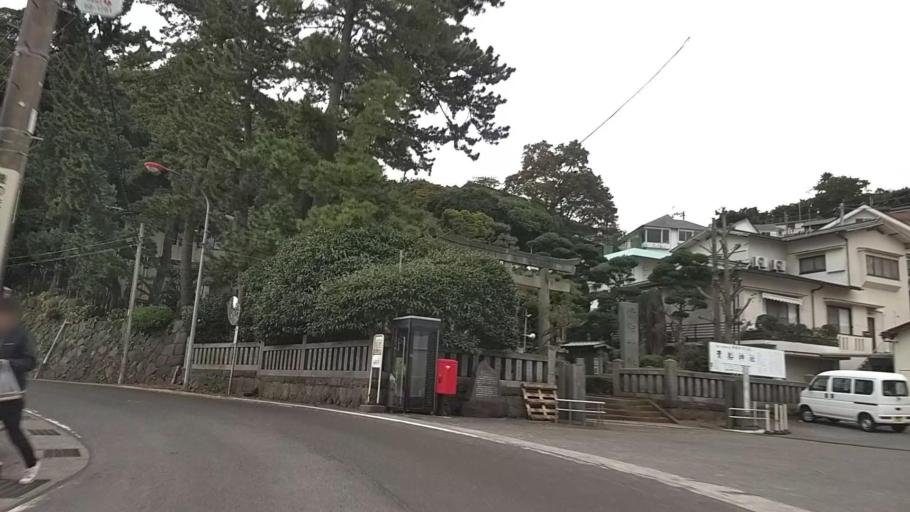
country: JP
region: Kanagawa
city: Yugawara
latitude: 35.1504
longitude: 139.1456
